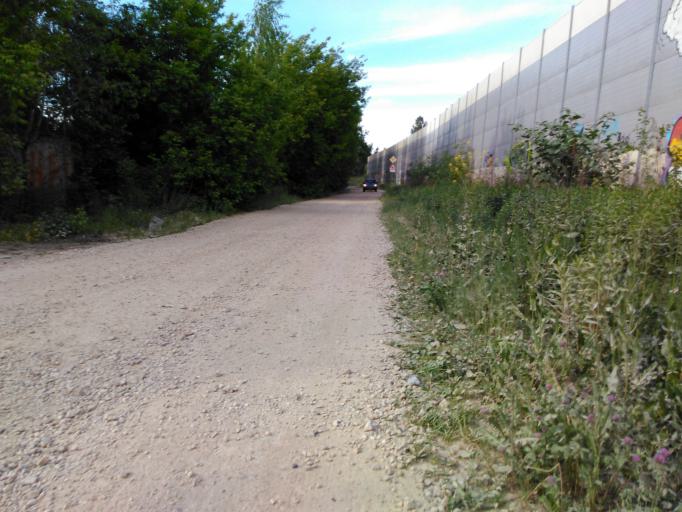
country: RU
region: Moskovskaya
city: Vishnyakovskiye Dachi
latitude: 55.7561
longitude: 38.1399
